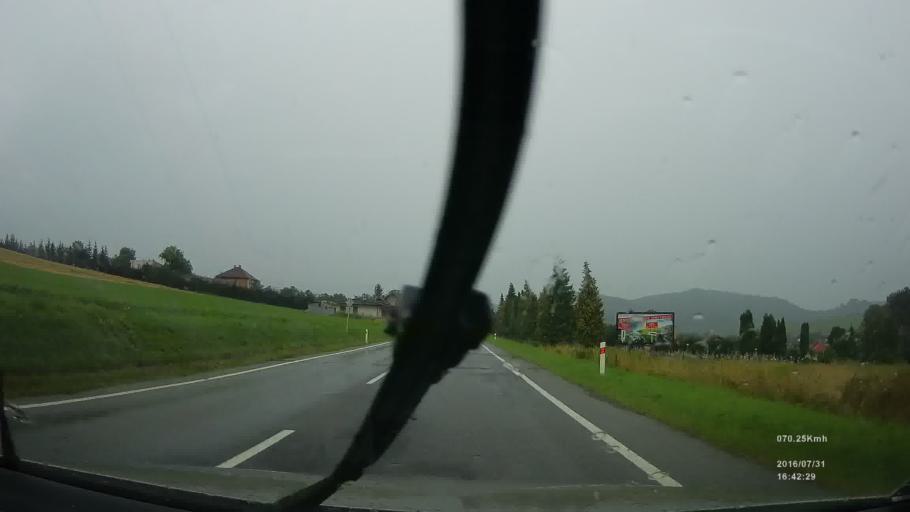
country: SK
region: Presovsky
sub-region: Okres Presov
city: Presov
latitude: 49.0933
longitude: 21.3118
